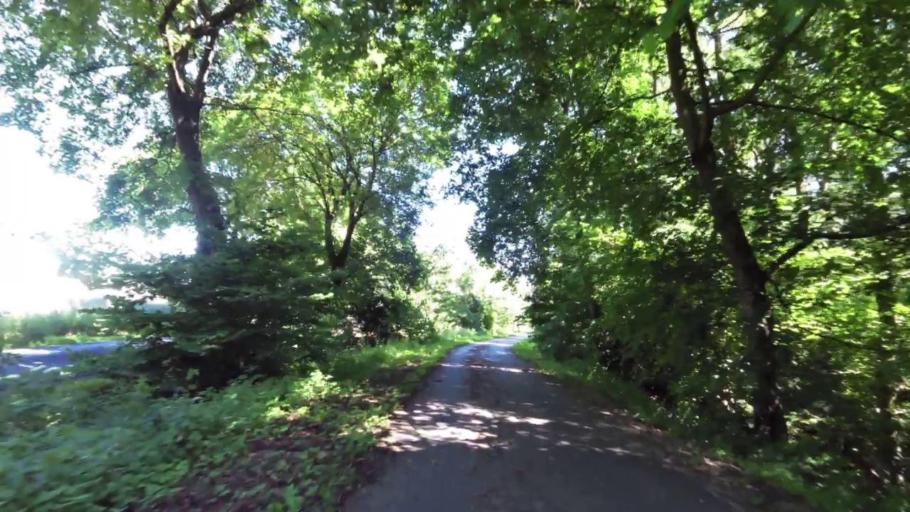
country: PL
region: West Pomeranian Voivodeship
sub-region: Powiat kolobrzeski
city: Goscino
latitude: 54.0336
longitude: 15.6878
